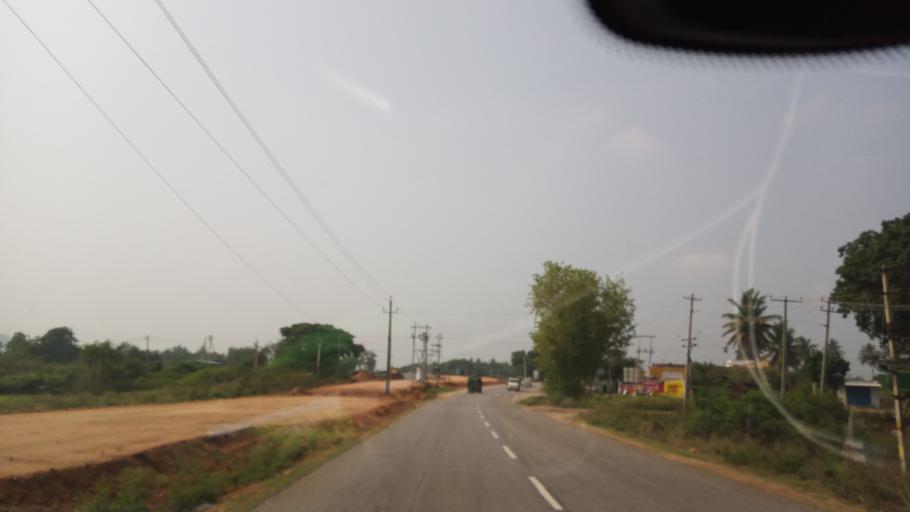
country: IN
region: Karnataka
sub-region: Mandya
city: Pandavapura
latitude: 12.5263
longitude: 76.6719
